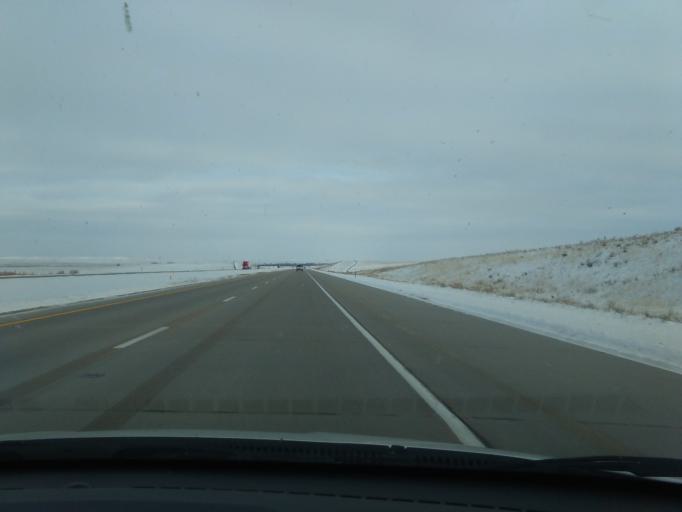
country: US
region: Nebraska
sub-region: Deuel County
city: Chappell
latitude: 41.1132
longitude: -102.5935
